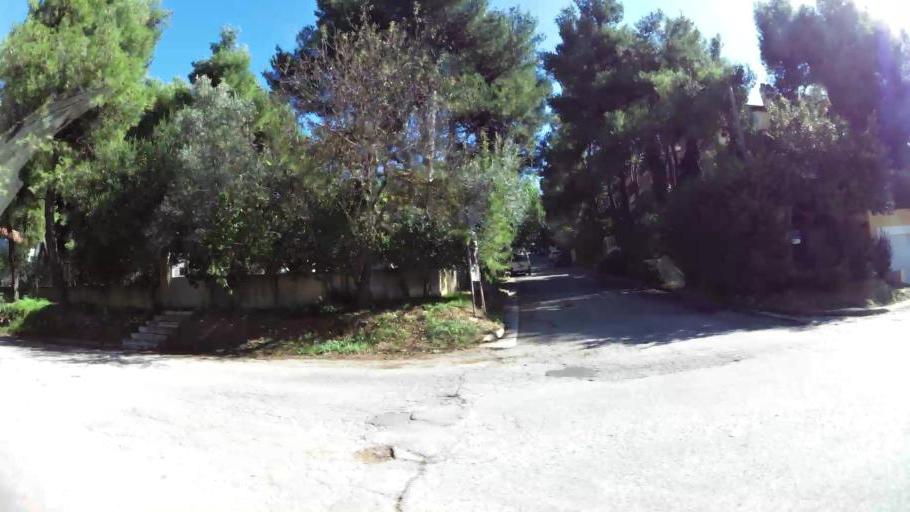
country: GR
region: Attica
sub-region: Nomarchia Anatolikis Attikis
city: Drosia
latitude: 38.1104
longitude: 23.8663
